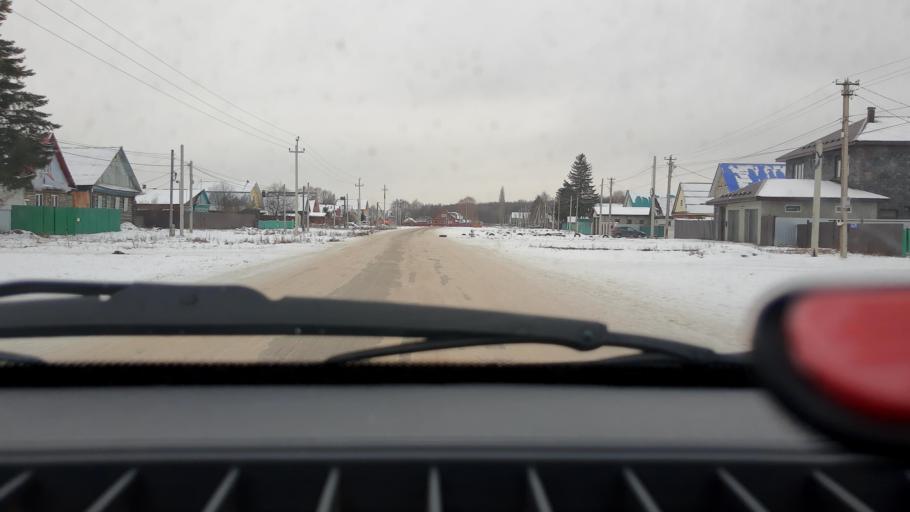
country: RU
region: Bashkortostan
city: Mikhaylovka
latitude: 54.7757
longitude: 55.8267
